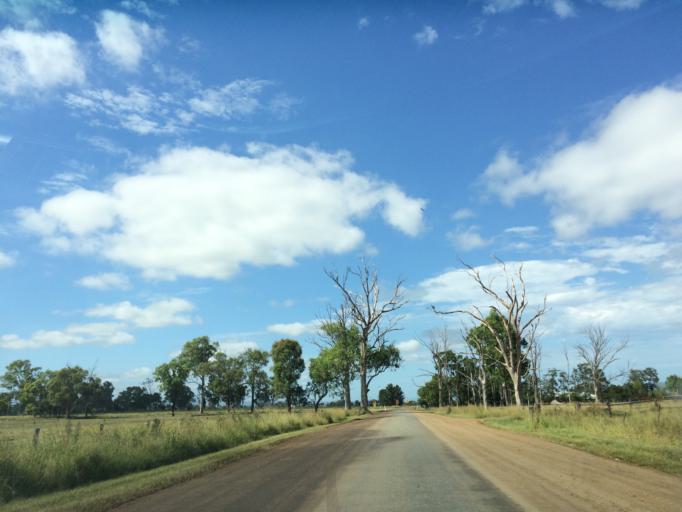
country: AU
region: Queensland
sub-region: Logan
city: Cedar Vale
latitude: -27.8778
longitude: 152.9556
